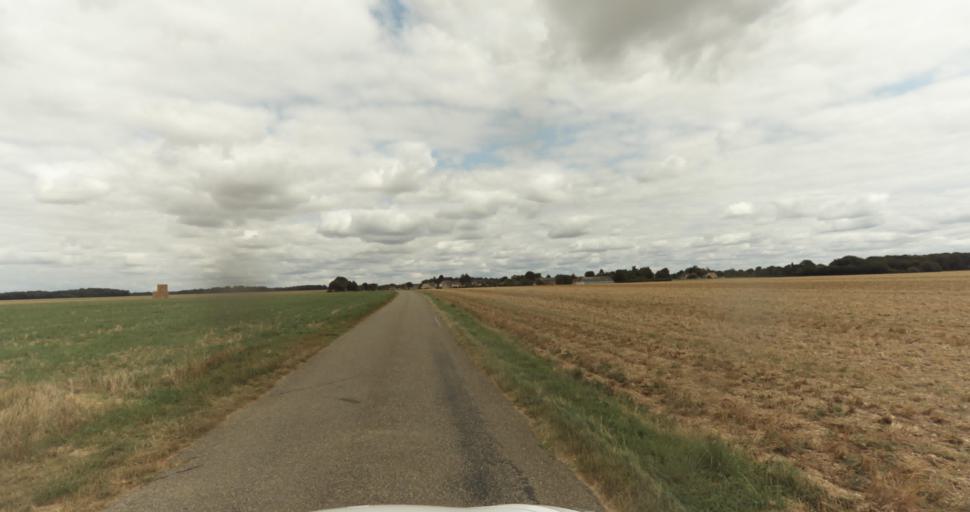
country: FR
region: Haute-Normandie
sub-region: Departement de l'Eure
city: Saint-Germain-sur-Avre
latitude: 48.7982
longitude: 1.2579
